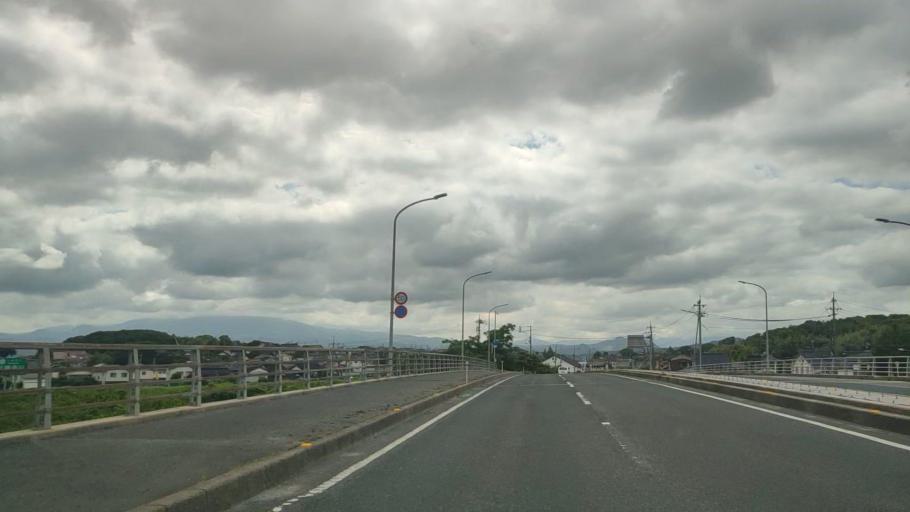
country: JP
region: Tottori
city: Yonago
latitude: 35.4081
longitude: 133.3632
